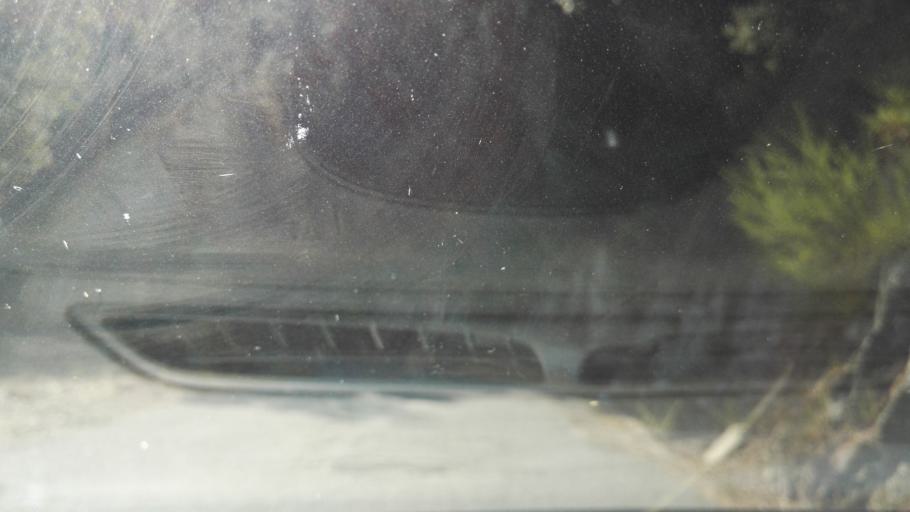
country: IT
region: Calabria
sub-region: Provincia di Vibo-Valentia
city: Nardodipace
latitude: 38.4594
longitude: 16.3494
